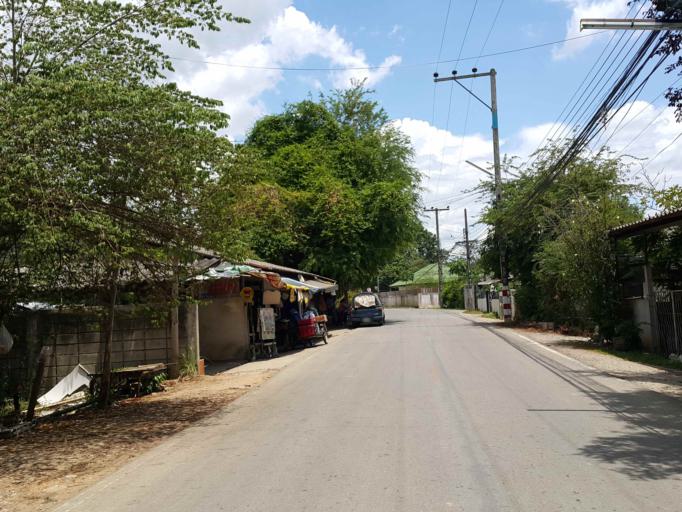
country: TH
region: Chiang Mai
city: Saraphi
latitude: 18.7351
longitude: 98.9964
